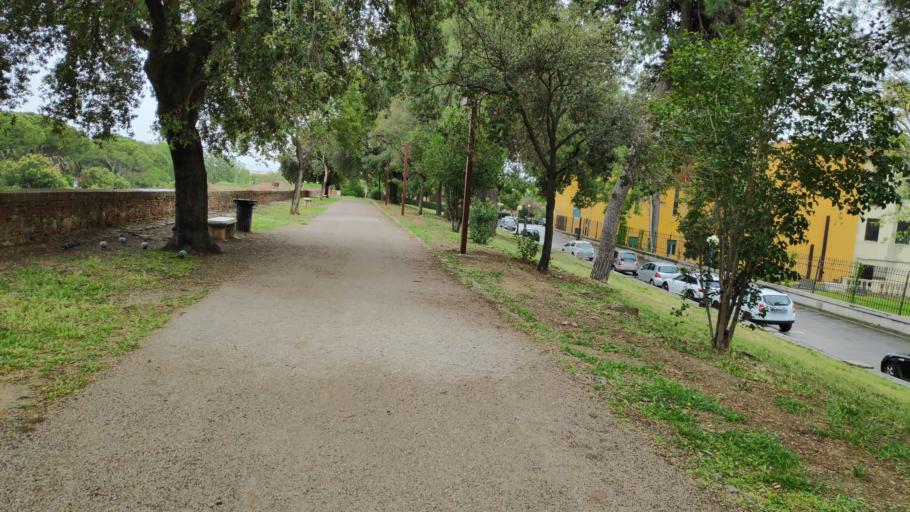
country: IT
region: Tuscany
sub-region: Provincia di Grosseto
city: Grosseto
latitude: 42.7627
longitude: 11.1147
